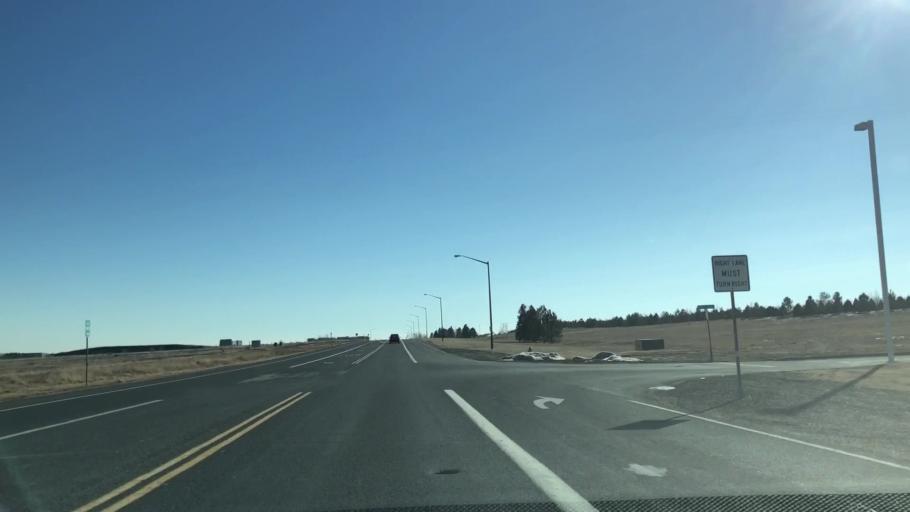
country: US
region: Colorado
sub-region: Weld County
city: Windsor
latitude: 40.4483
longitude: -104.9824
